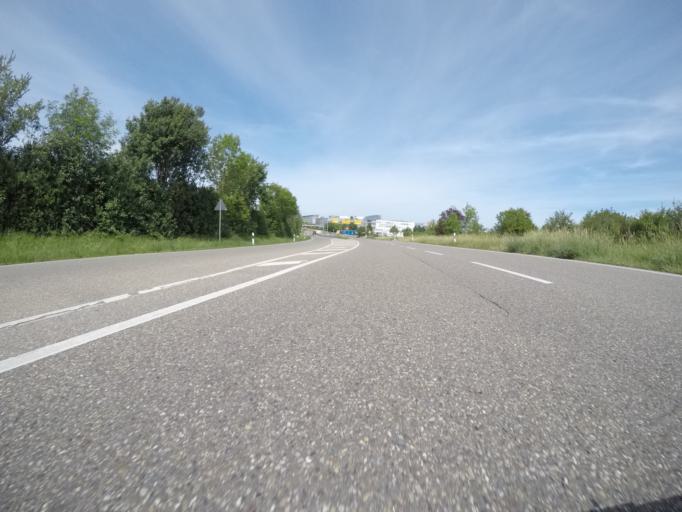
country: DE
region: Baden-Wuerttemberg
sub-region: Regierungsbezirk Stuttgart
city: Korntal
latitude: 48.8172
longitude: 9.1002
